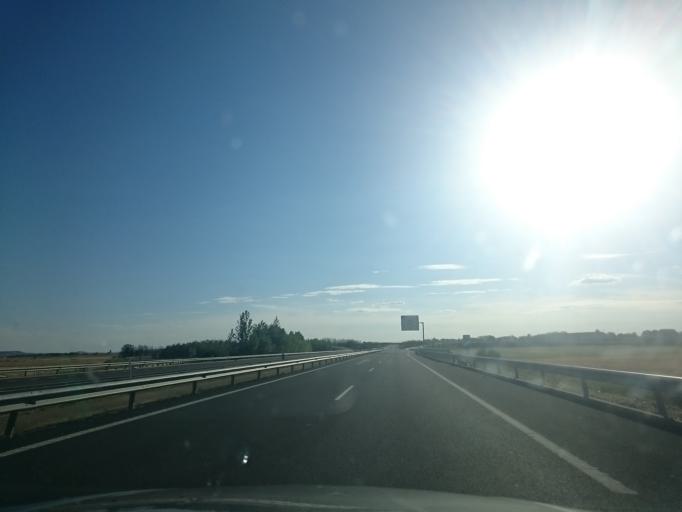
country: ES
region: Castille and Leon
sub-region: Provincia de Burgos
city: Sasamon
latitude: 42.3964
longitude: -4.0652
